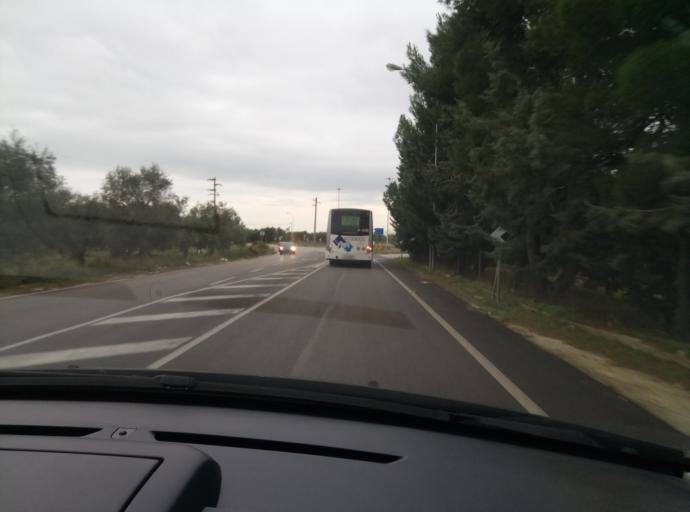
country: IT
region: Apulia
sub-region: Provincia di Bari
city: Acquaviva delle Fonti
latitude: 40.9079
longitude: 16.8496
